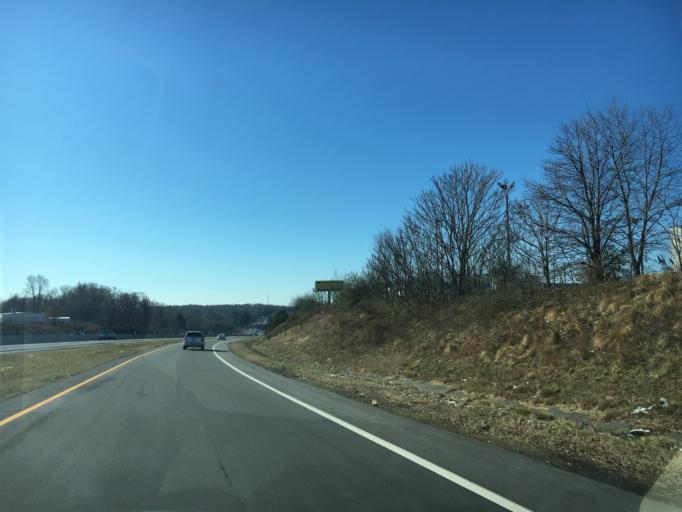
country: US
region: South Carolina
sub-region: Spartanburg County
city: Wellford
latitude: 34.9134
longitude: -82.1093
